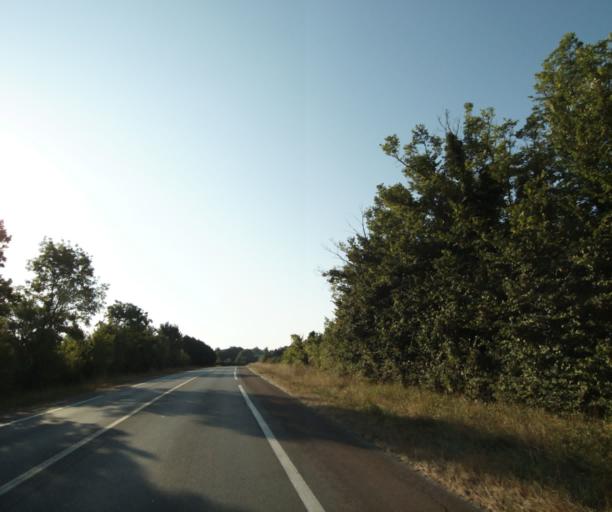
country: FR
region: Poitou-Charentes
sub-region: Departement de la Charente-Maritime
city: Tonnay-Charente
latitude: 45.9503
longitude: -0.8692
